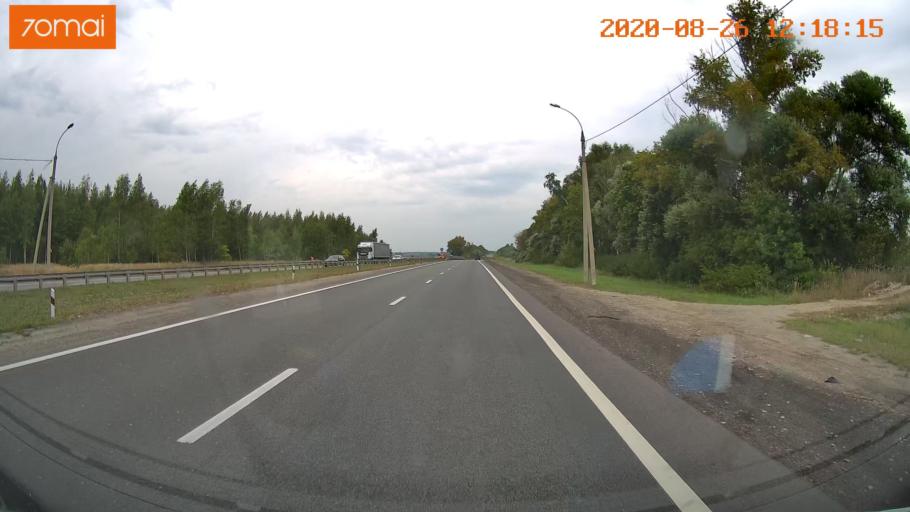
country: RU
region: Rjazan
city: Murmino
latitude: 54.4711
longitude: 40.0209
